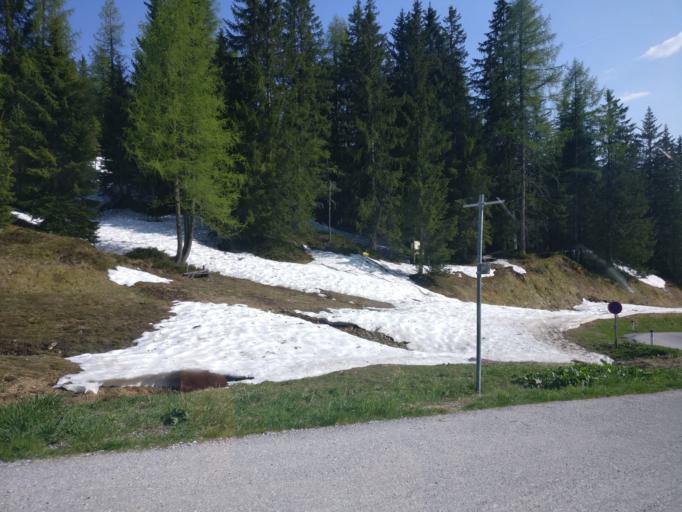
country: AT
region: Salzburg
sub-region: Politischer Bezirk Sankt Johann im Pongau
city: Muhlbach am Hochkonig
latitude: 47.4096
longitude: 13.1289
